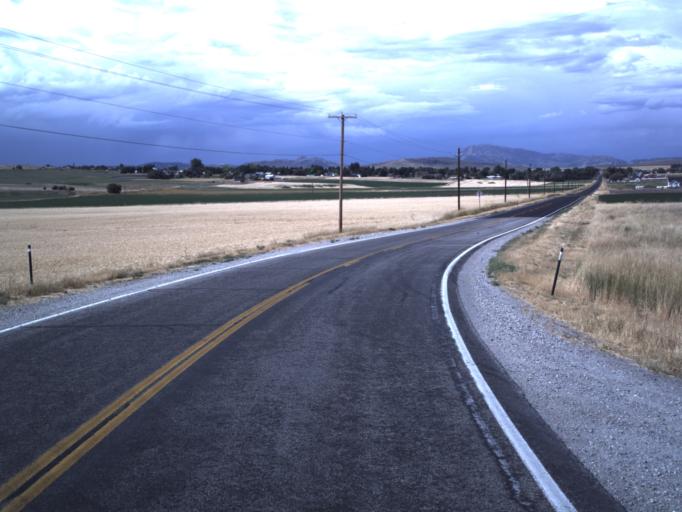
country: US
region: Utah
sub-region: Cache County
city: Benson
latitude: 41.8988
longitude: -112.0457
